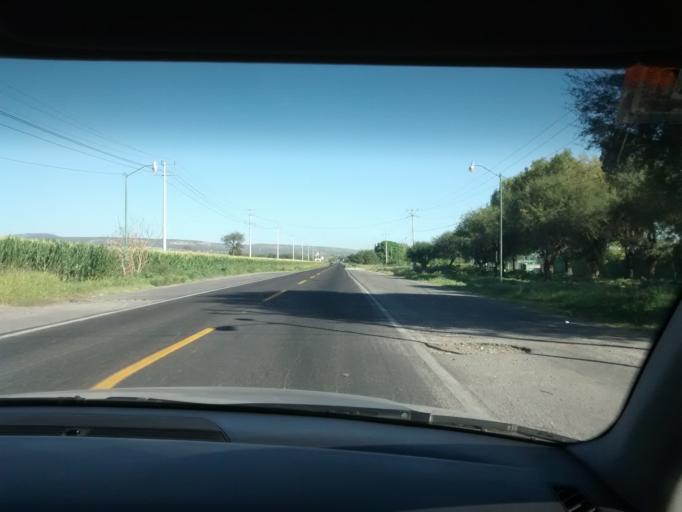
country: MX
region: Puebla
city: San Bartolo Teontepec
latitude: 18.5428
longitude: -97.5400
